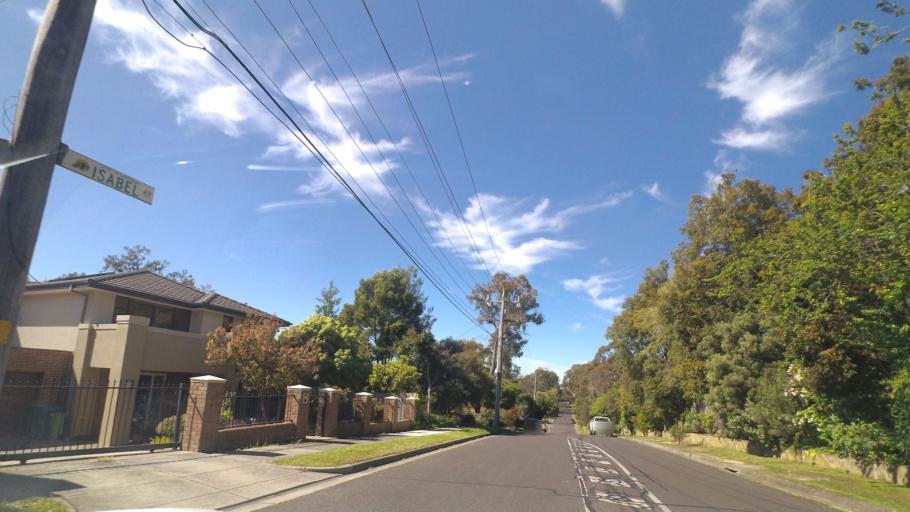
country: AU
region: Victoria
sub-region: Maroondah
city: Ringwood East
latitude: -37.8174
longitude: 145.2562
